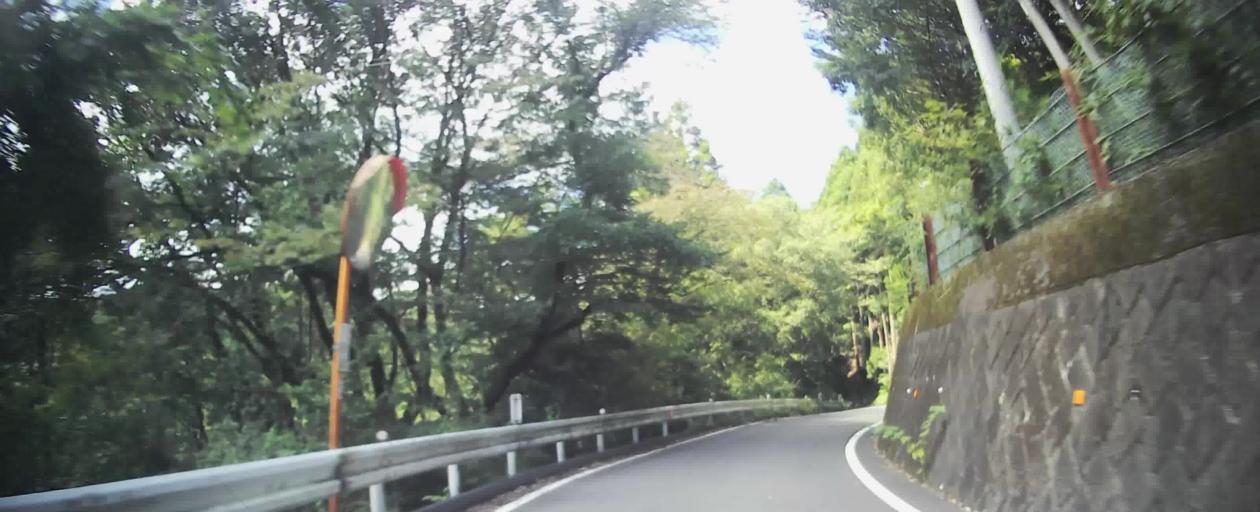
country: JP
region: Gunma
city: Kanekomachi
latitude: 36.4452
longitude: 138.9067
